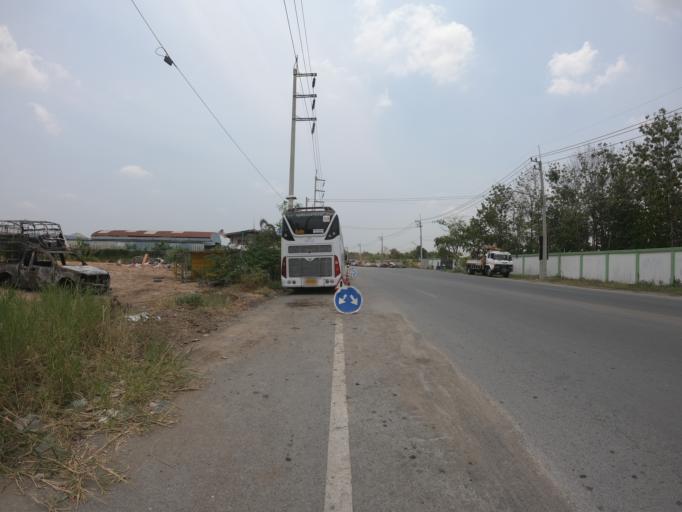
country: TH
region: Phra Nakhon Si Ayutthaya
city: Ban Bang Kadi Pathum Thani
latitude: 14.0101
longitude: 100.5715
